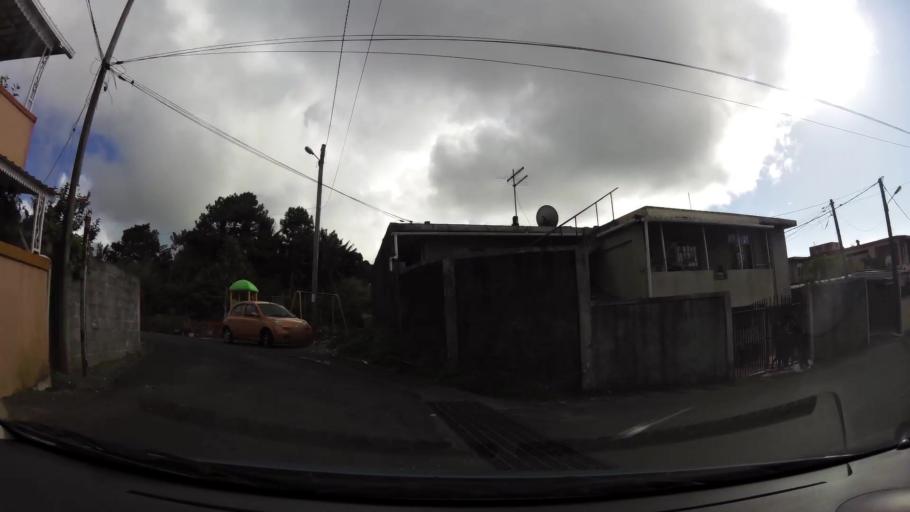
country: MU
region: Plaines Wilhems
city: Curepipe
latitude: -20.3298
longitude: 57.5187
